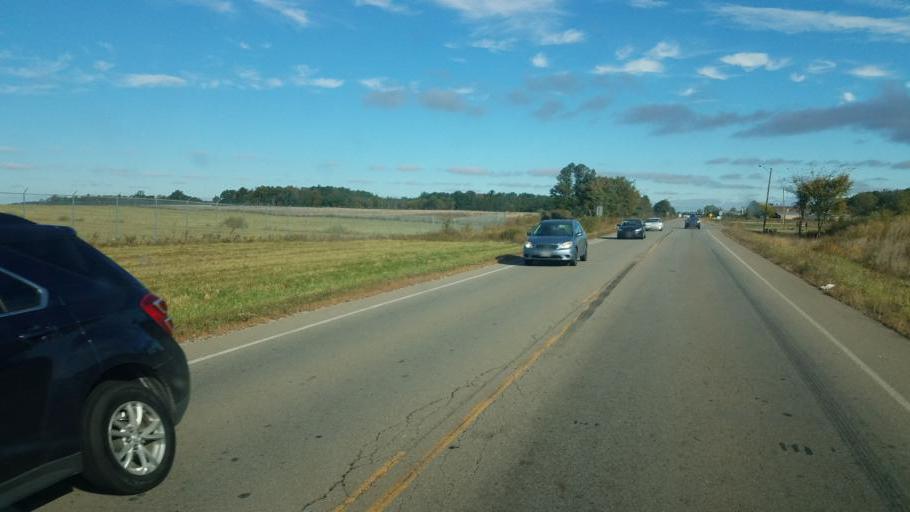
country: US
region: Ohio
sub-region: Richland County
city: Lincoln Heights
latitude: 40.8134
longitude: -82.5003
